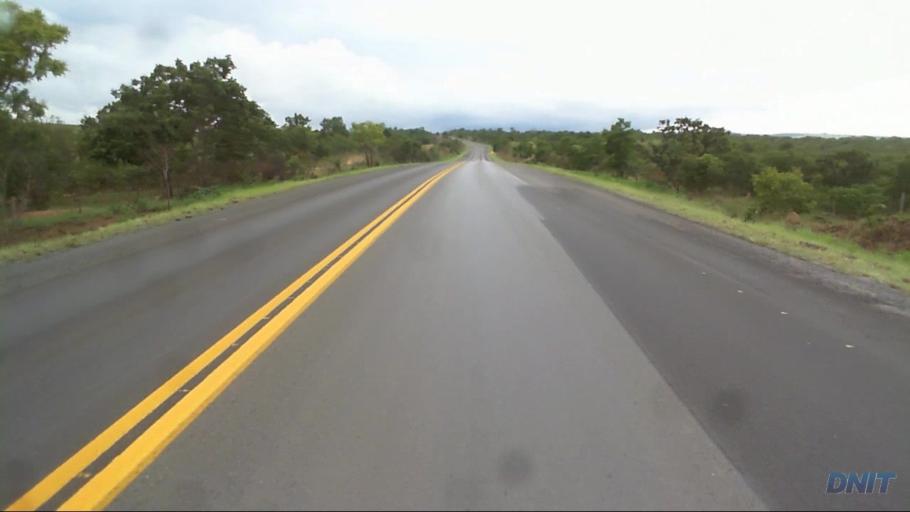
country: BR
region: Goias
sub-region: Padre Bernardo
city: Padre Bernardo
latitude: -15.2139
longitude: -48.5777
